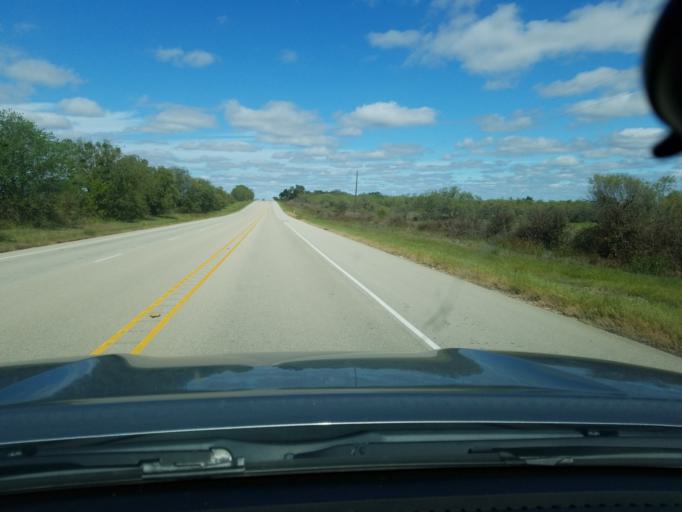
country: US
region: Texas
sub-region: Hamilton County
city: Hamilton
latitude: 31.5647
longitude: -98.1588
